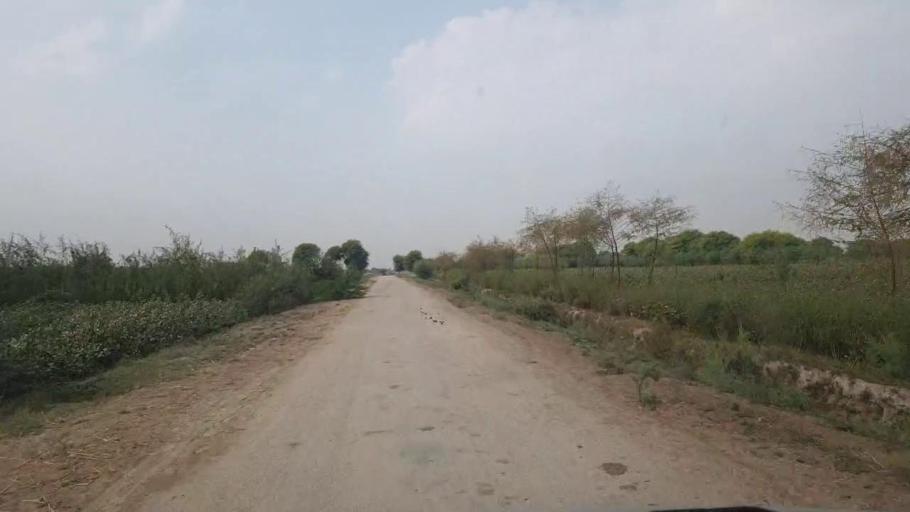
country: PK
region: Sindh
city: Talhar
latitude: 24.8623
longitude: 68.8330
